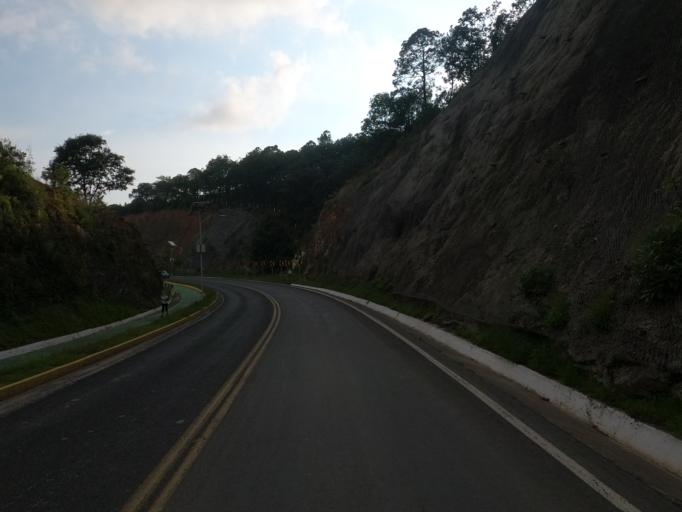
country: MX
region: Mexico
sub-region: Valle de Bravo
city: Colonia Rincon Villa del Valle
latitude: 19.2098
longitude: -100.1116
